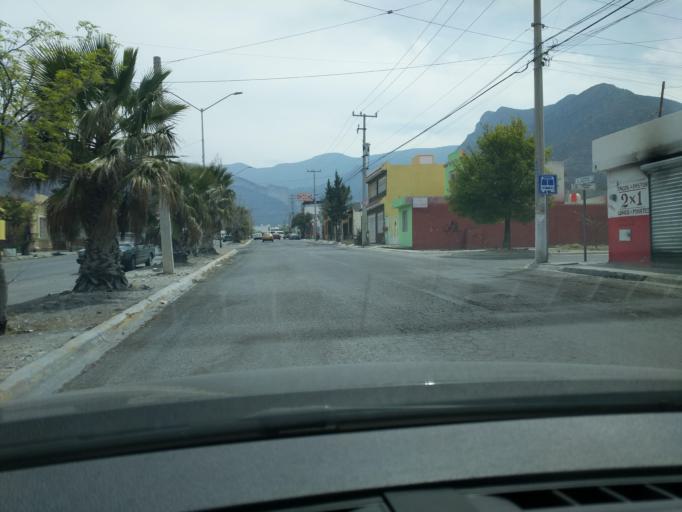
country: MX
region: Coahuila
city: Saltillo
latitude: 25.3503
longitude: -101.0112
